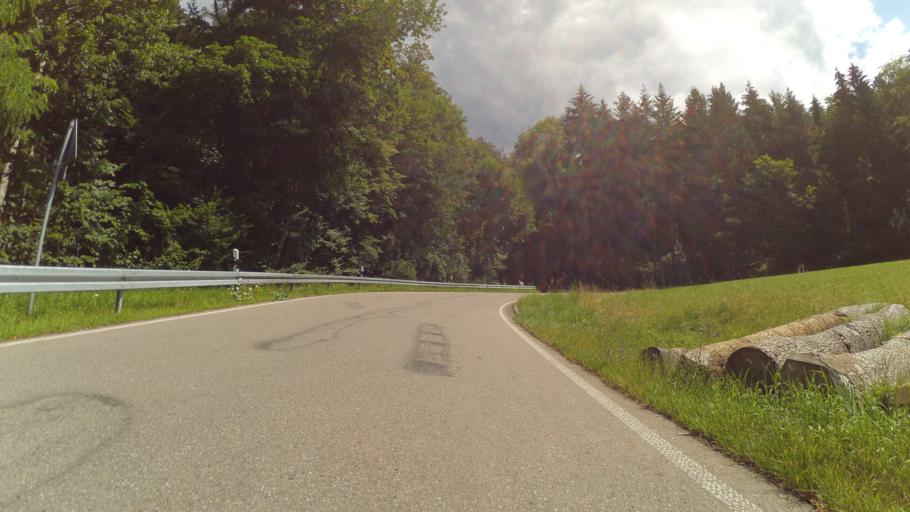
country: DE
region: Baden-Wuerttemberg
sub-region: Freiburg Region
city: Badenweiler
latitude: 47.8165
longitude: 7.6808
